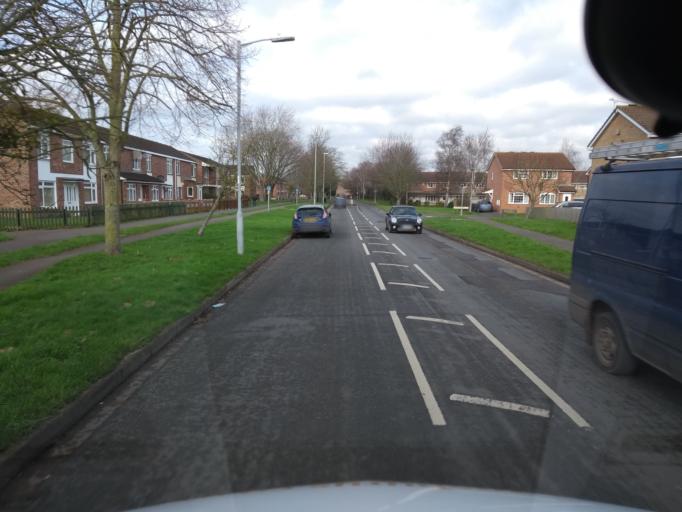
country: GB
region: England
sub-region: Somerset
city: Taunton
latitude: 51.0103
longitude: -3.0753
